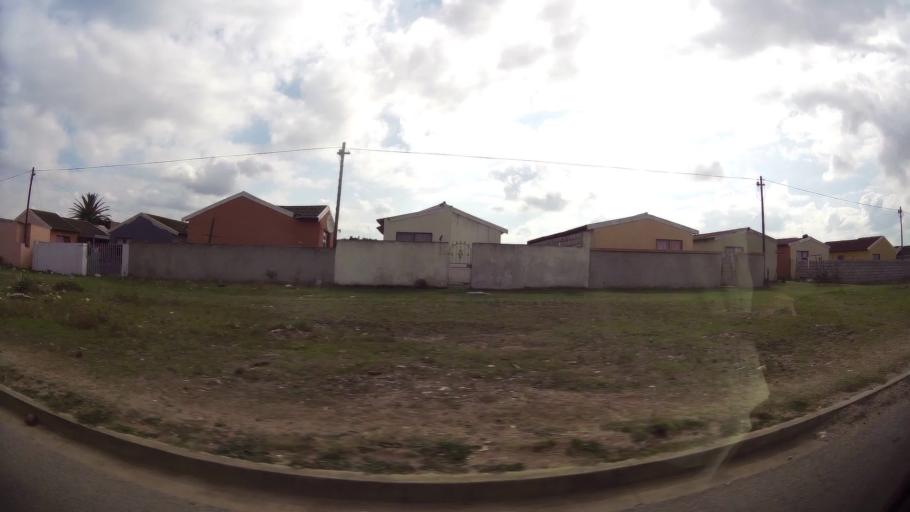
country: ZA
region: Eastern Cape
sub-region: Nelson Mandela Bay Metropolitan Municipality
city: Port Elizabeth
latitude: -33.8200
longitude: 25.5928
